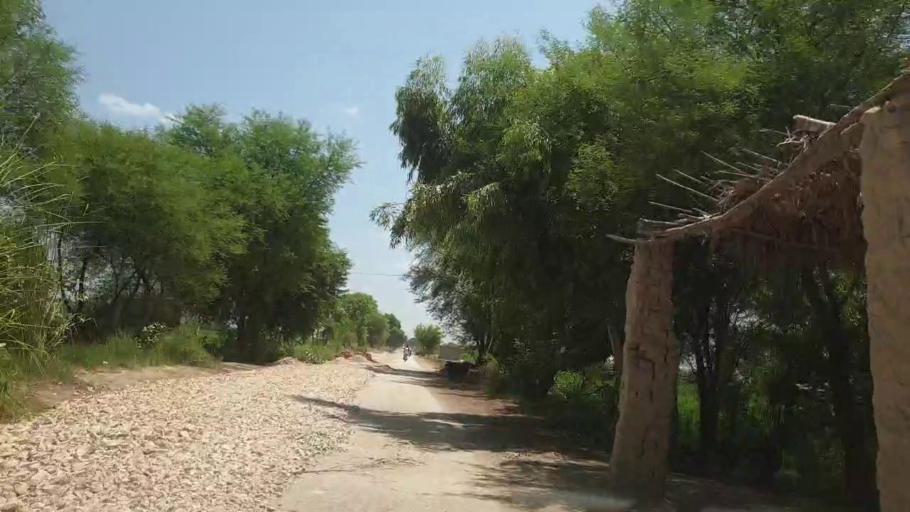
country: PK
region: Sindh
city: Pano Aqil
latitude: 27.6659
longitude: 69.1916
